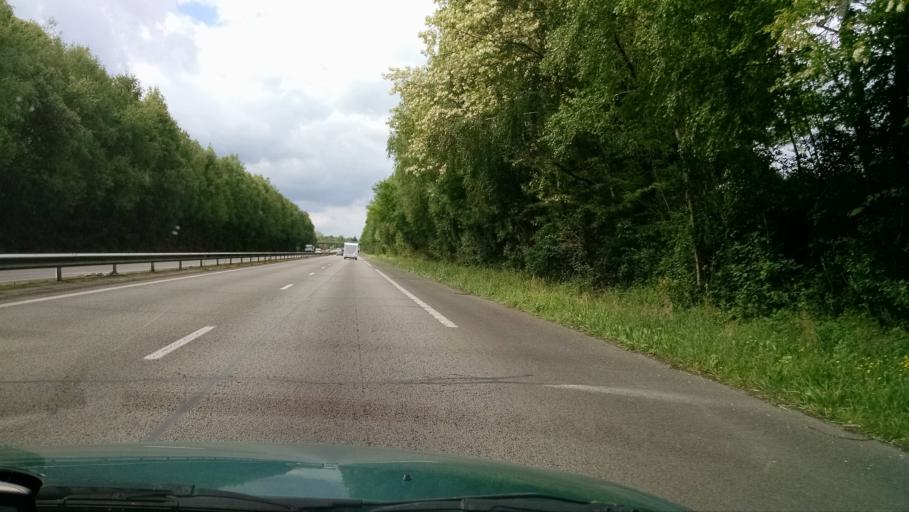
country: FR
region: Pays de la Loire
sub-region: Departement de la Loire-Atlantique
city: Treillieres
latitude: 47.3261
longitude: -1.6473
